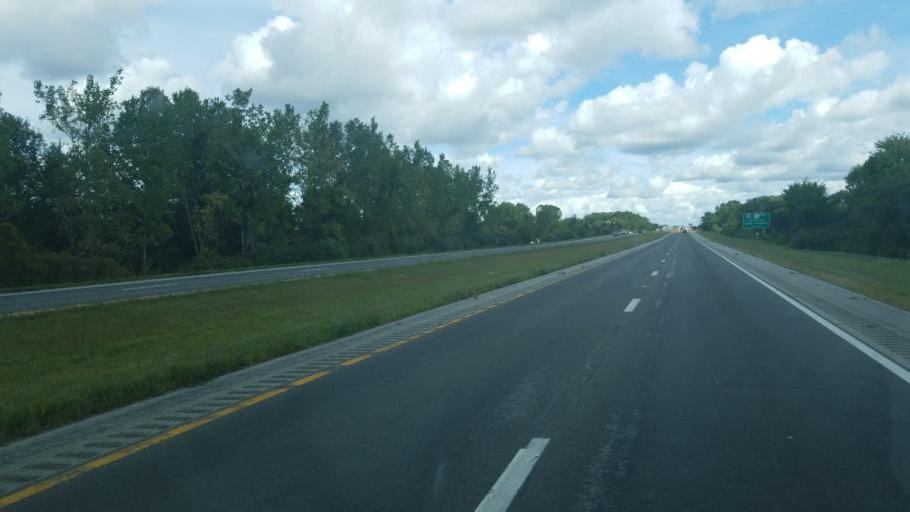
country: US
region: Ohio
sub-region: Lorain County
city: North Ridgeville
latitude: 41.3683
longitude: -82.0031
